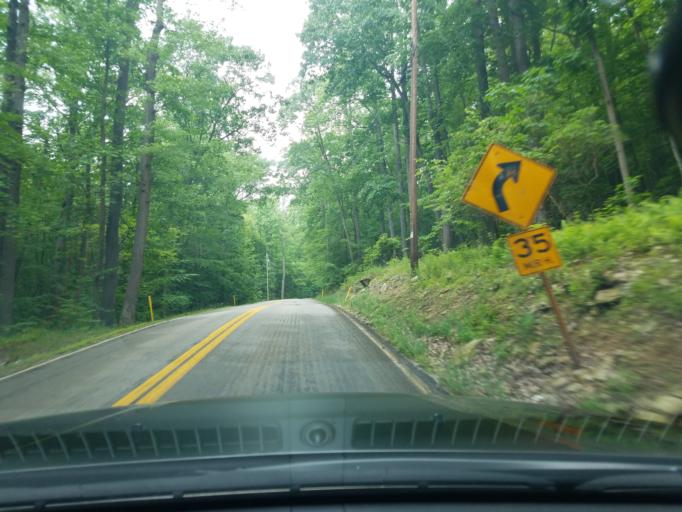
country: US
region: Pennsylvania
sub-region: Fayette County
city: Bear Rocks
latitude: 40.1853
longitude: -79.3829
